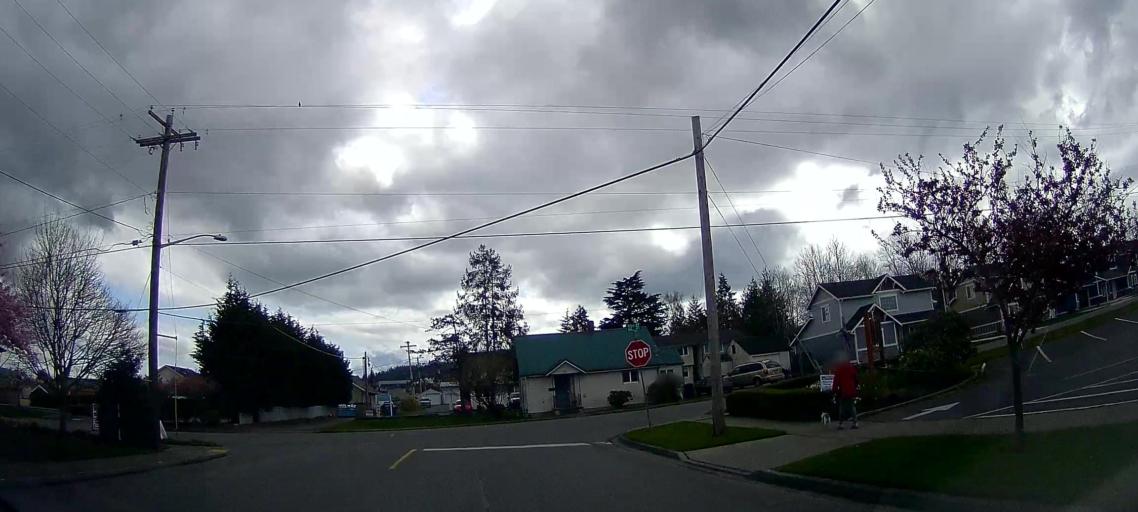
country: US
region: Washington
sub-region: Skagit County
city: Anacortes
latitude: 48.5047
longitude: -122.6144
